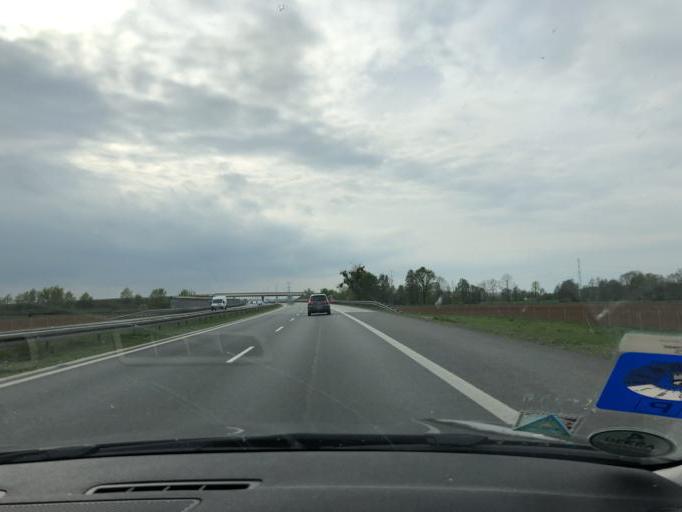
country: PL
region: Opole Voivodeship
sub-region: Powiat brzeski
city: Lewin Brzeski
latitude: 50.7083
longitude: 17.6061
